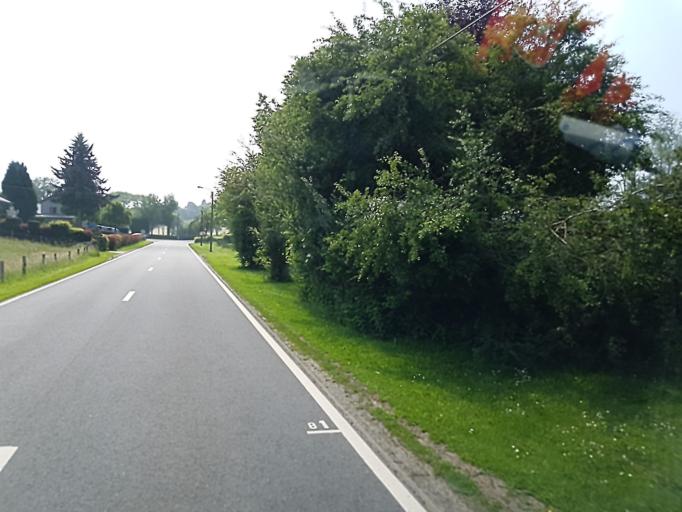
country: BE
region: Wallonia
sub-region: Province de Liege
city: Lierneux
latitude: 50.3227
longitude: 5.7421
